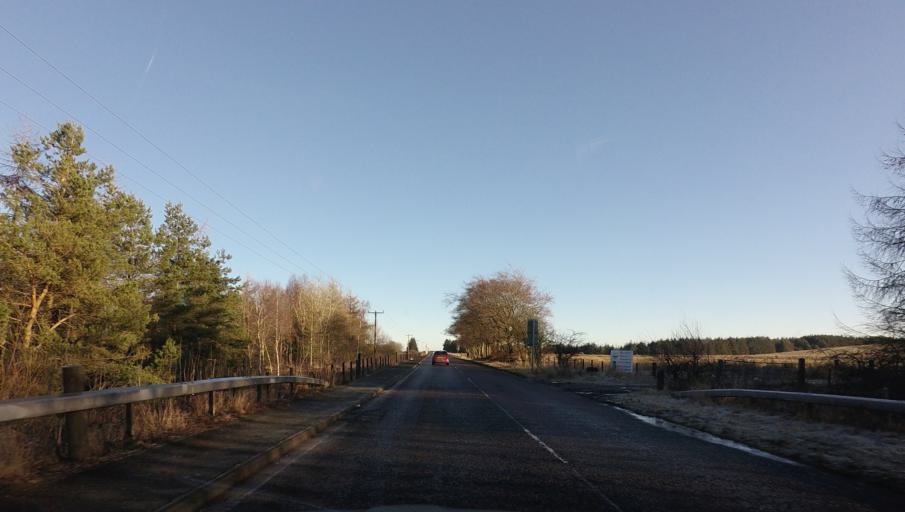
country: GB
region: Scotland
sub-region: West Lothian
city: Blackburn
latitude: 55.8316
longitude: -3.6466
